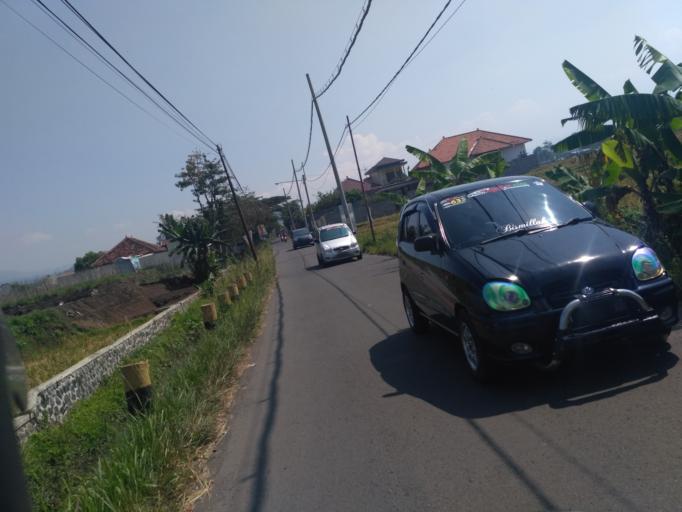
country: ID
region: East Java
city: Batu
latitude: -7.9067
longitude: 112.5847
